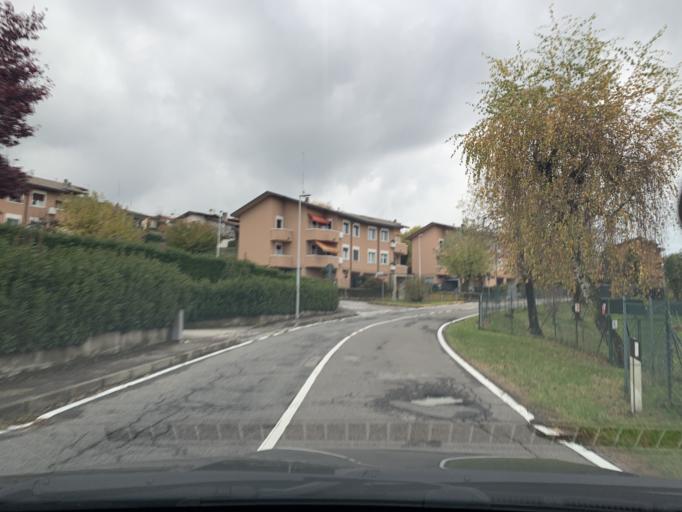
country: IT
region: Lombardy
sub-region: Provincia di Como
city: Casnate Con Bernate
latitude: 45.7637
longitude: 9.0715
